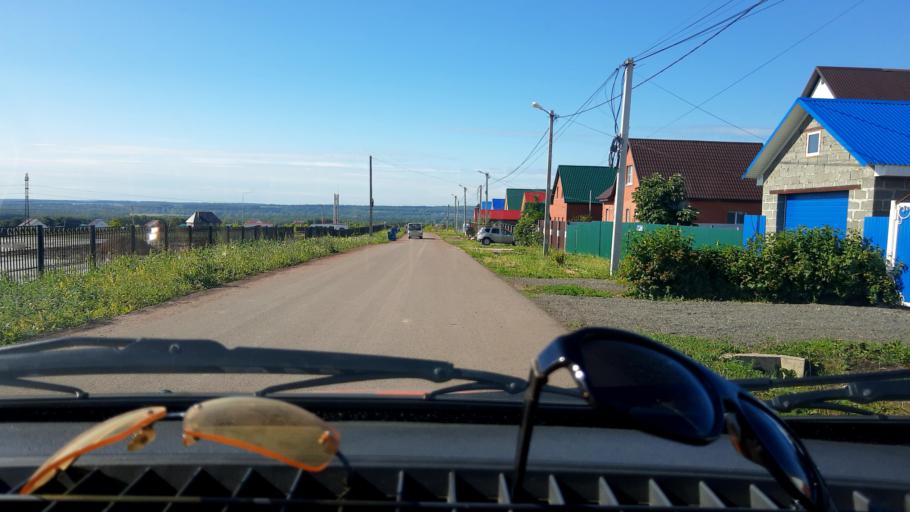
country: RU
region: Bashkortostan
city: Avdon
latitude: 54.6527
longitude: 55.7376
